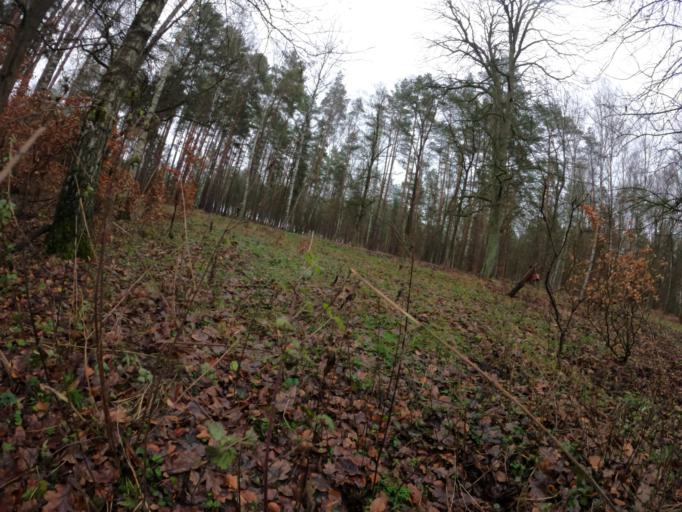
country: PL
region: West Pomeranian Voivodeship
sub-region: Powiat mysliborski
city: Debno
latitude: 52.7509
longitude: 14.7755
